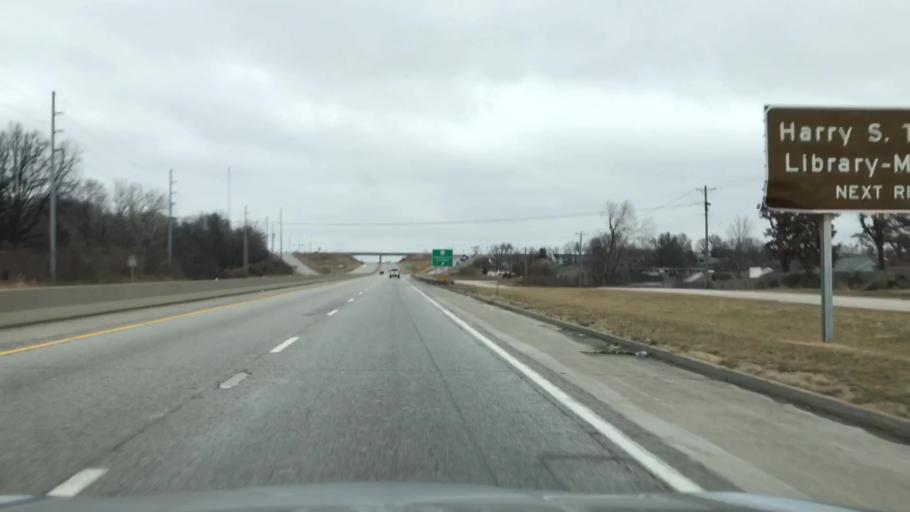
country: US
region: Missouri
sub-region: Jackson County
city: East Independence
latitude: 39.1113
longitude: -94.3826
